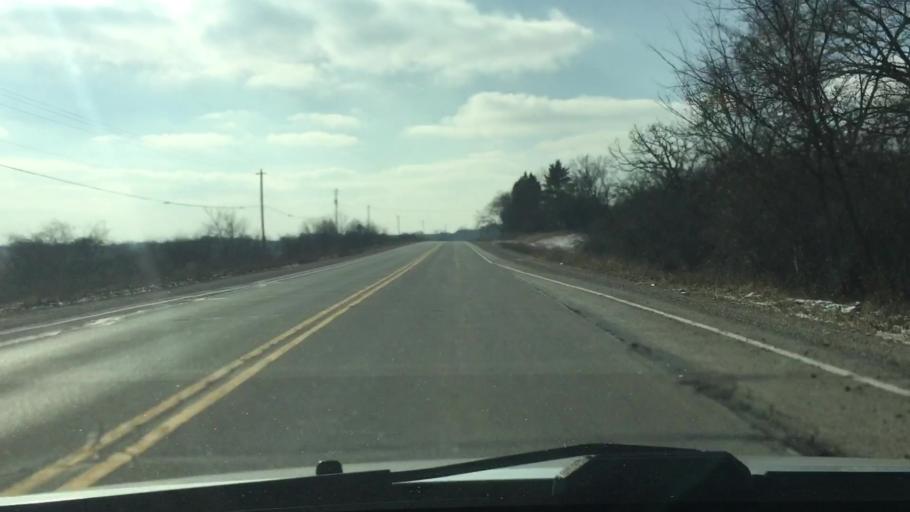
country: US
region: Wisconsin
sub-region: Waukesha County
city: North Prairie
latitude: 42.9274
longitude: -88.4279
